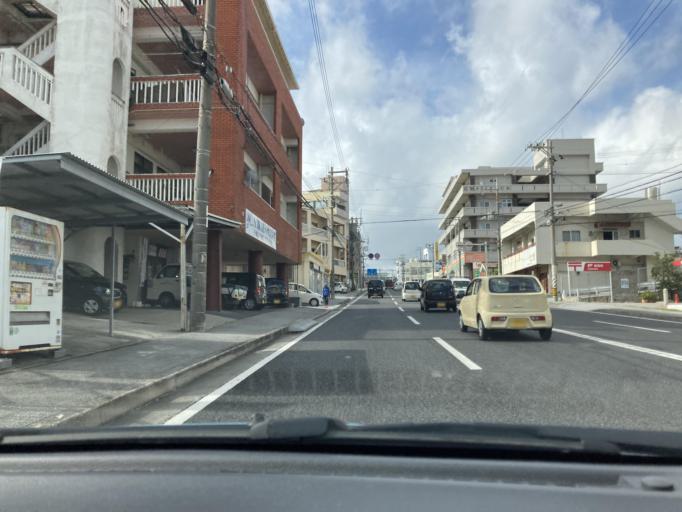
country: JP
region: Okinawa
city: Ginowan
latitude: 26.2560
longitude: 127.7404
